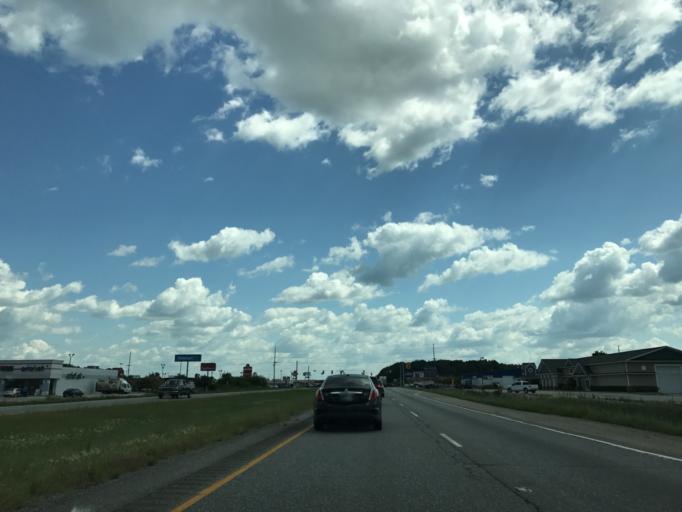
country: US
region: Indiana
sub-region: Marshall County
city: Plymouth
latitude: 41.3614
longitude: -86.3321
